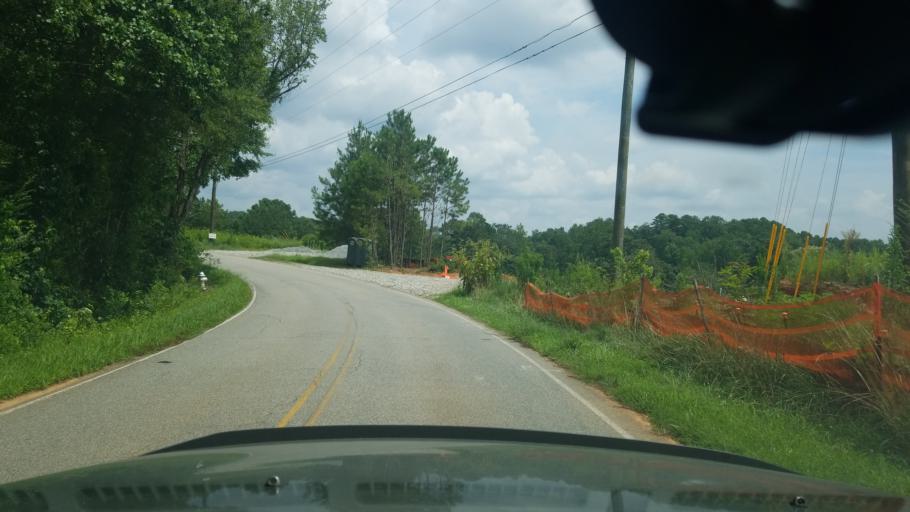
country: US
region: Georgia
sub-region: Forsyth County
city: Cumming
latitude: 34.2713
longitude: -84.2204
